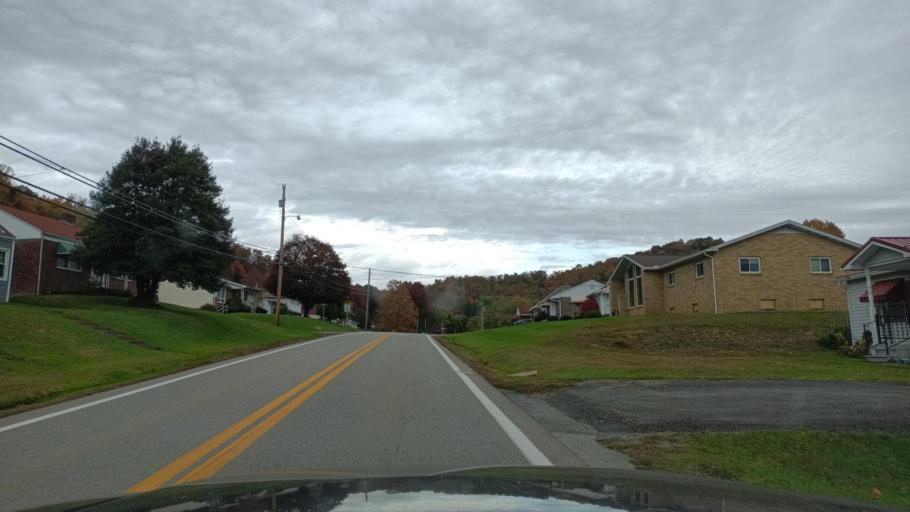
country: US
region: West Virginia
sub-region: Taylor County
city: Grafton
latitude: 39.3510
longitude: -79.9973
